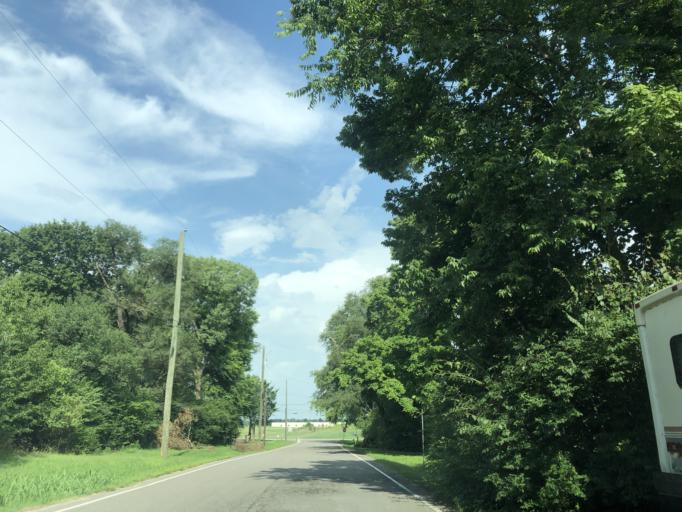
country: US
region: Tennessee
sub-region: Davidson County
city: Oak Hill
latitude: 36.1083
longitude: -86.6911
